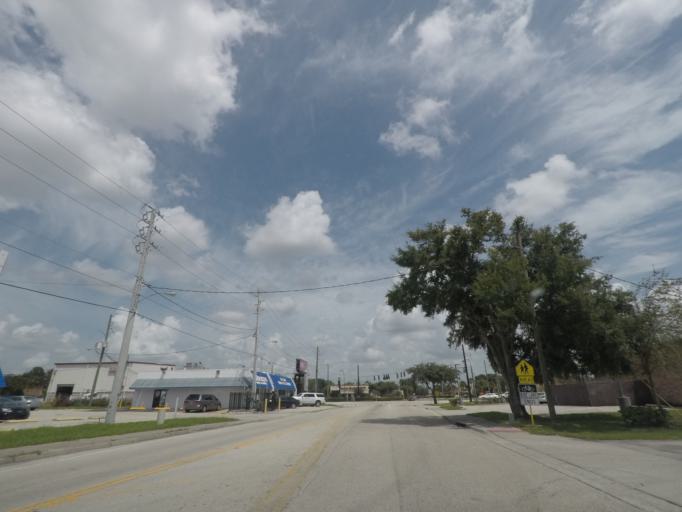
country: US
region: Florida
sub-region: Osceola County
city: Kissimmee
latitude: 28.3036
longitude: -81.4368
